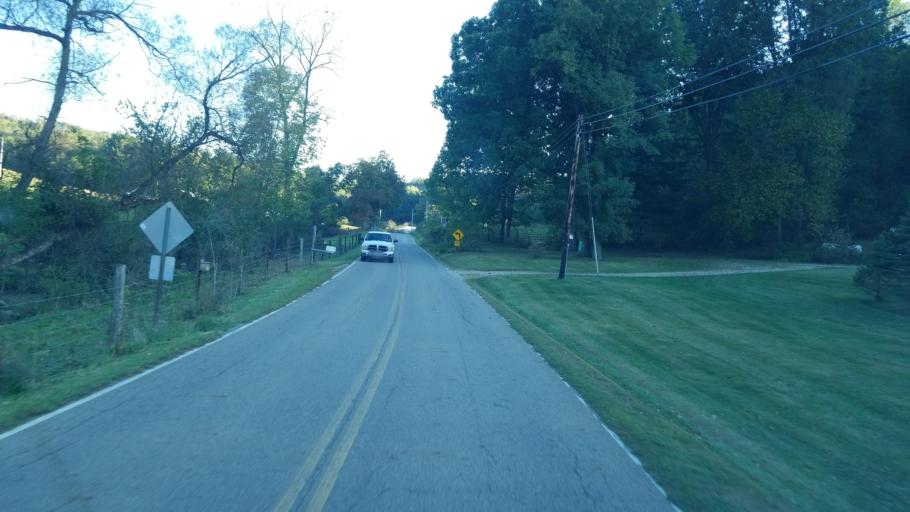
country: US
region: Ohio
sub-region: Licking County
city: Utica
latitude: 40.1659
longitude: -82.3858
